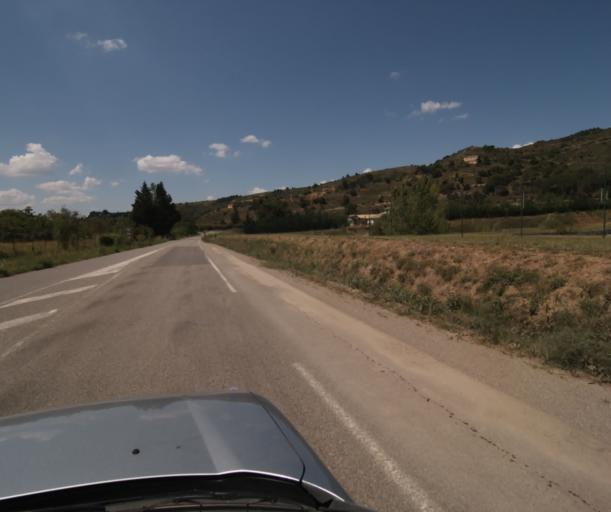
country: FR
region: Languedoc-Roussillon
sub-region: Departement de l'Aude
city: Limoux
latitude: 43.0435
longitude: 2.2450
